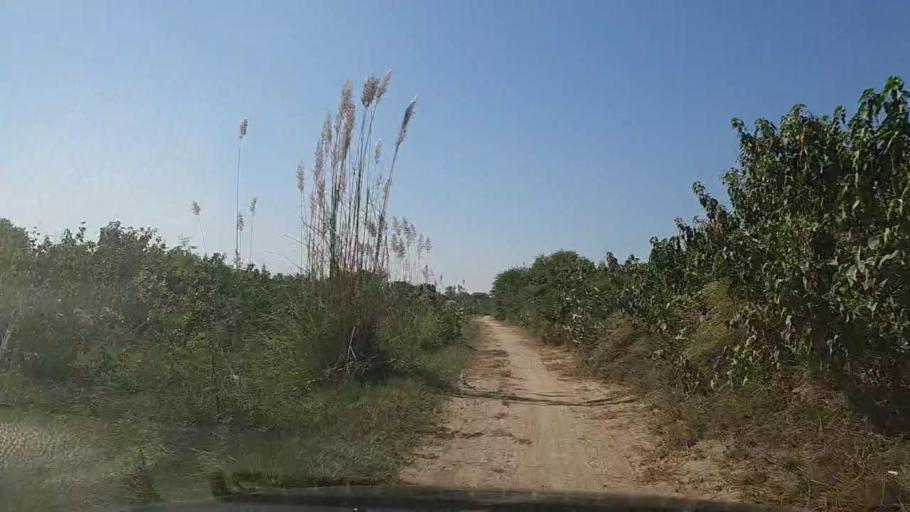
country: PK
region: Sindh
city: Mirpur Sakro
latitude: 24.5760
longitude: 67.7945
